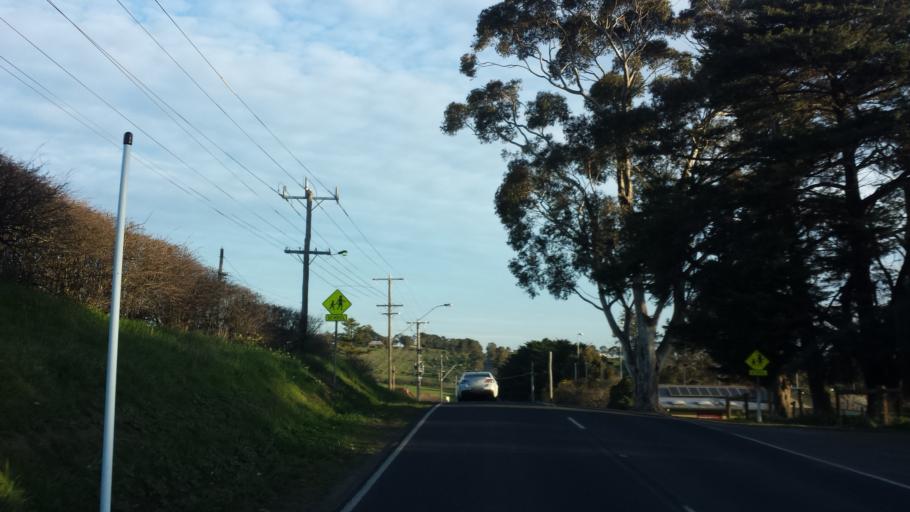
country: AU
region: Victoria
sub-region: Nillumbik
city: Research
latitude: -37.6900
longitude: 145.2159
